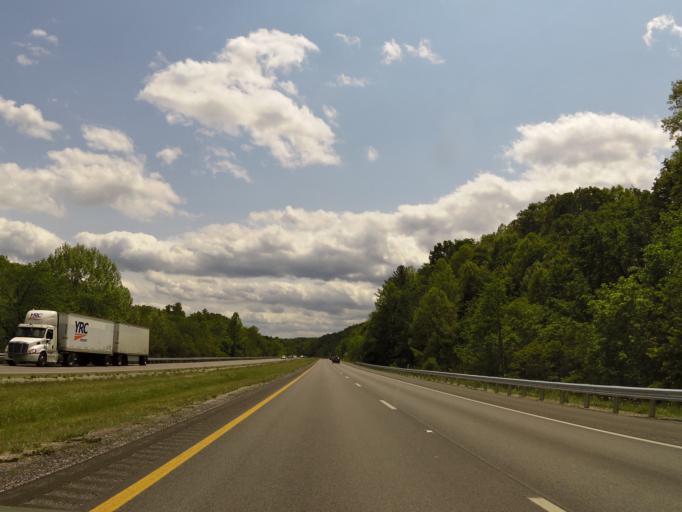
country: US
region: West Virginia
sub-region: Kanawha County
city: Sissonville
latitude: 38.6349
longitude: -81.6490
